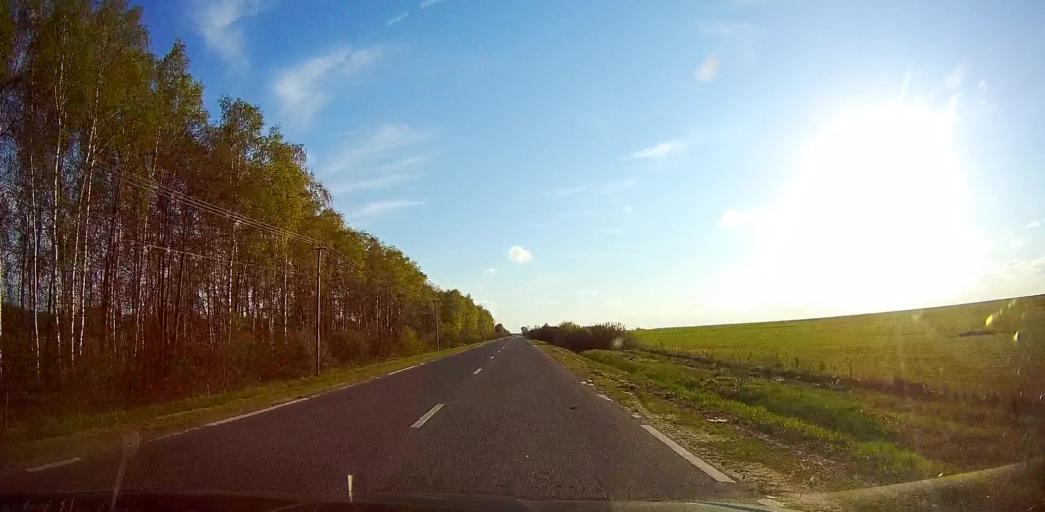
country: RU
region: Moskovskaya
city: Bronnitsy
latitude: 55.2895
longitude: 38.1945
